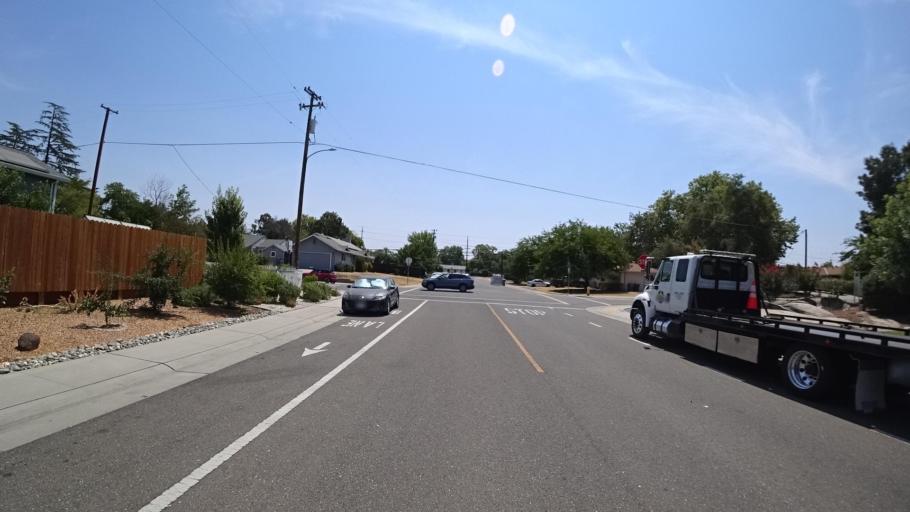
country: US
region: California
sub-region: Placer County
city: Rocklin
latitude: 38.7922
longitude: -121.2321
